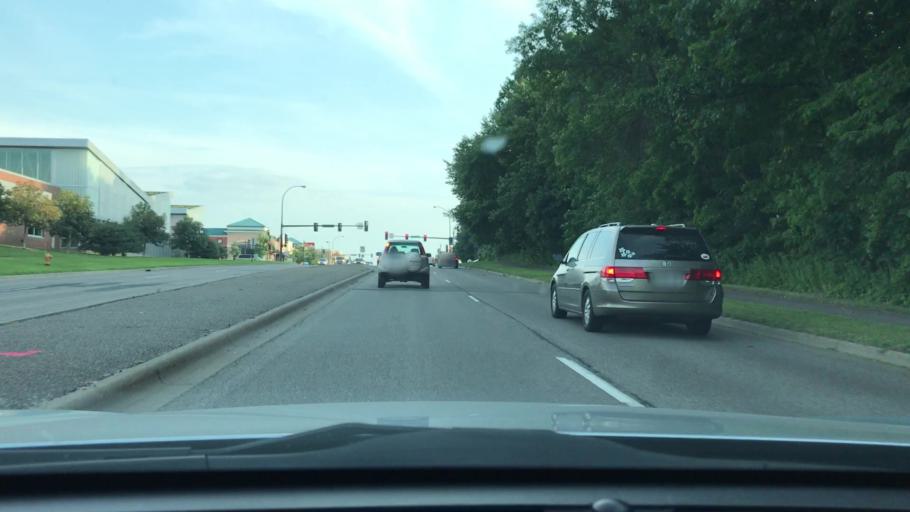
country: US
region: Minnesota
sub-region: Hennepin County
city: Plymouth
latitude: 45.0235
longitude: -93.4818
